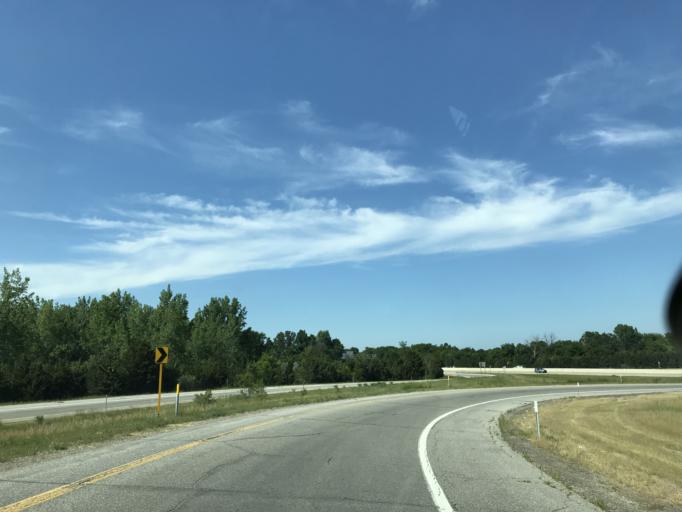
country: US
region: Michigan
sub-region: Bay County
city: Bay City
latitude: 43.5968
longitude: -83.9498
